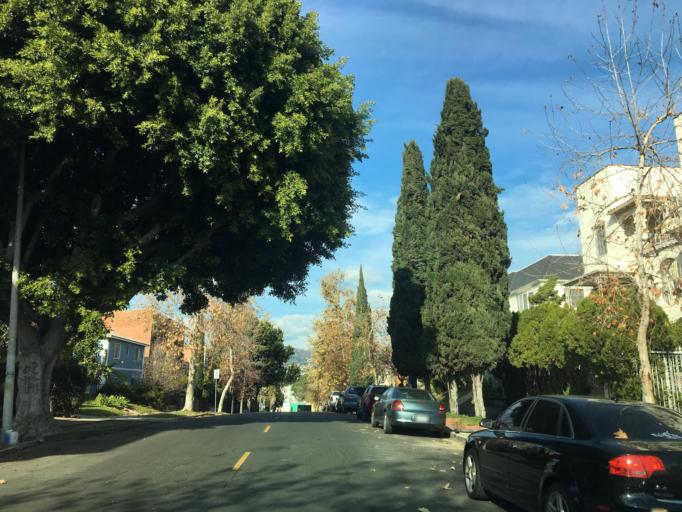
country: US
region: California
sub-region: Los Angeles County
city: Silver Lake
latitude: 34.0748
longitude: -118.2966
